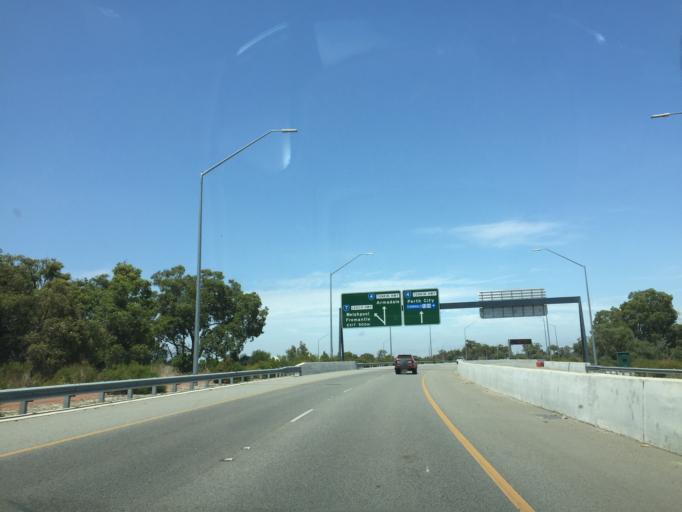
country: AU
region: Western Australia
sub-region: Belmont
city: Kewdale
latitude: -31.9612
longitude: 115.9671
